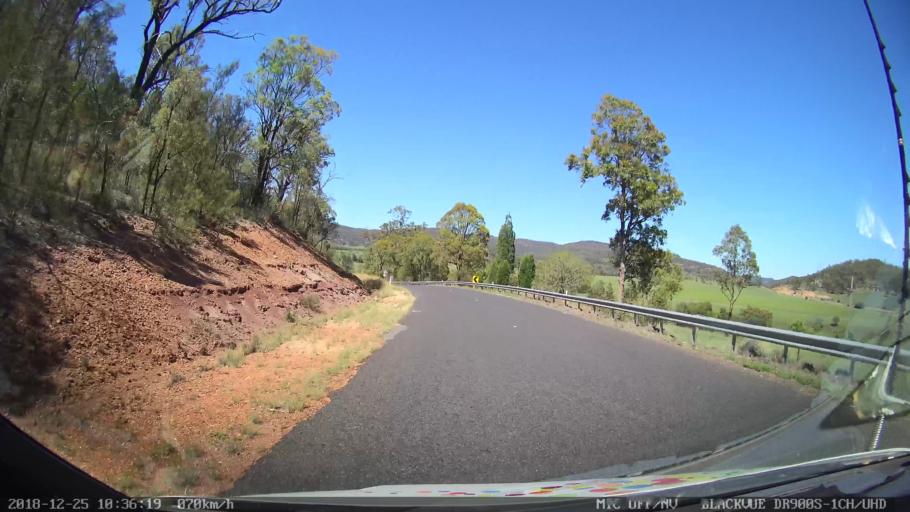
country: AU
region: New South Wales
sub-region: Upper Hunter Shire
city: Merriwa
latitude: -32.4026
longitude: 150.3860
